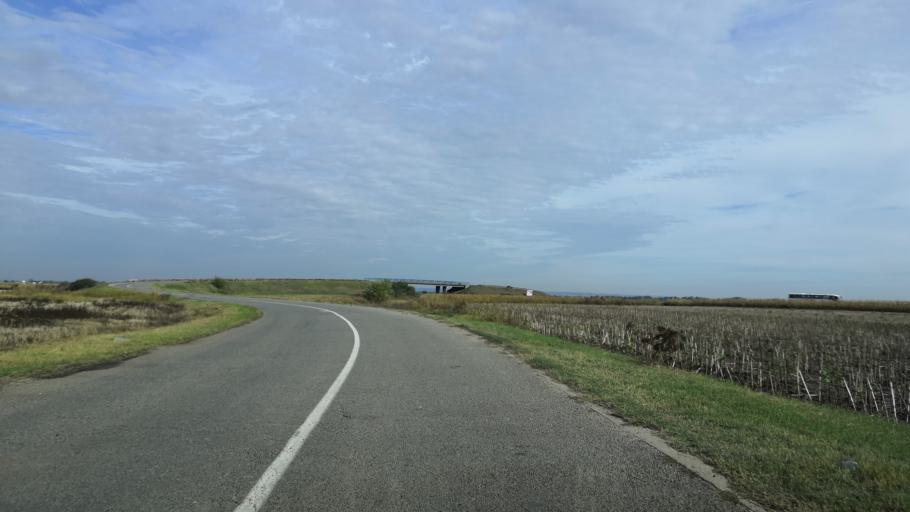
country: RS
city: Novi Karlovci
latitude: 45.0445
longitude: 20.1756
